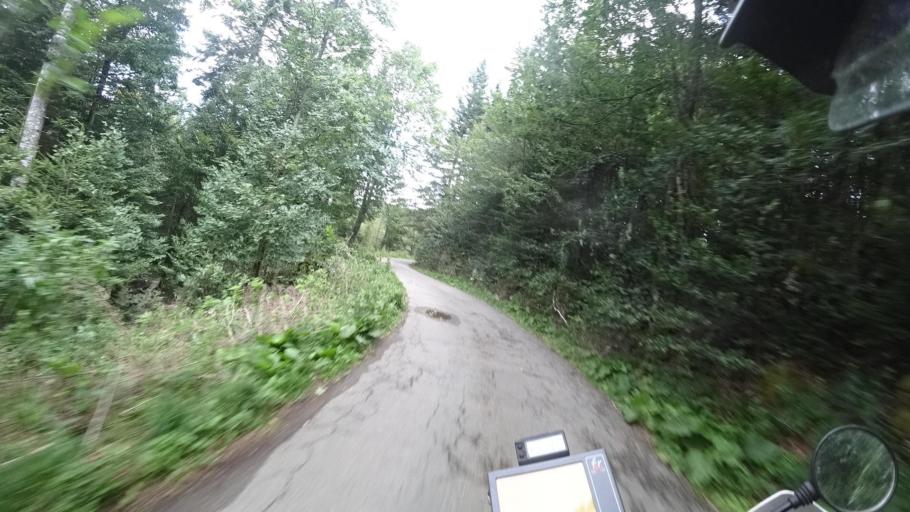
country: HR
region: Licko-Senjska
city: Senj
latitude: 45.1064
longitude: 14.9981
